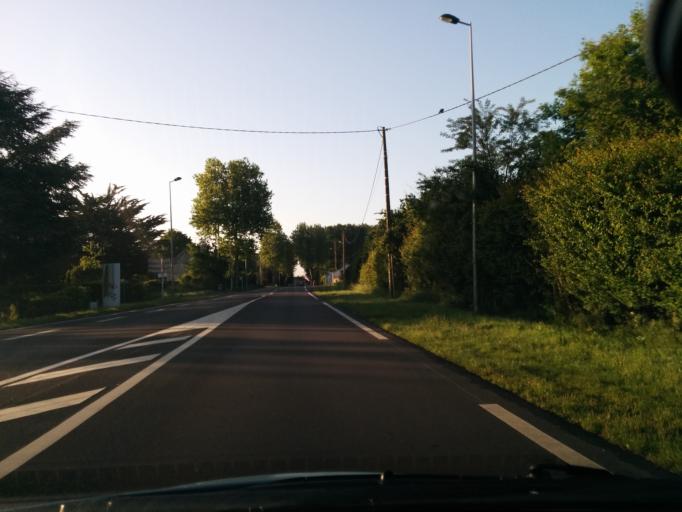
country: FR
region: Ile-de-France
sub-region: Departement des Yvelines
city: Freneuse
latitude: 49.0293
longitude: 1.6071
